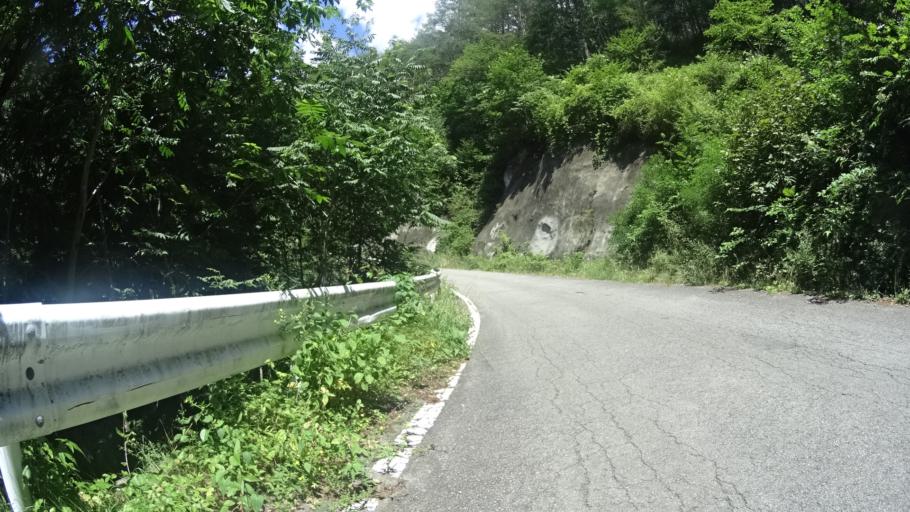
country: JP
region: Yamanashi
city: Enzan
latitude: 35.8188
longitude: 138.6540
